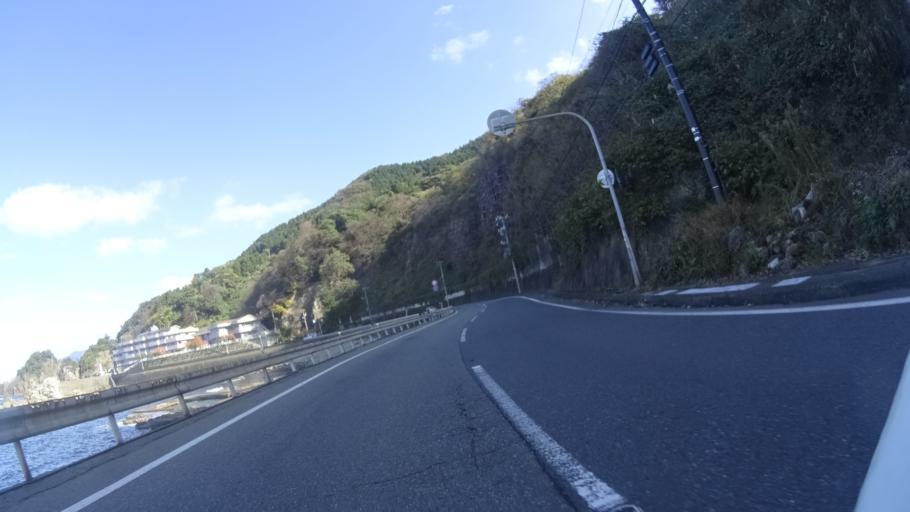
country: JP
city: Asahi
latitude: 35.8895
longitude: 135.9956
